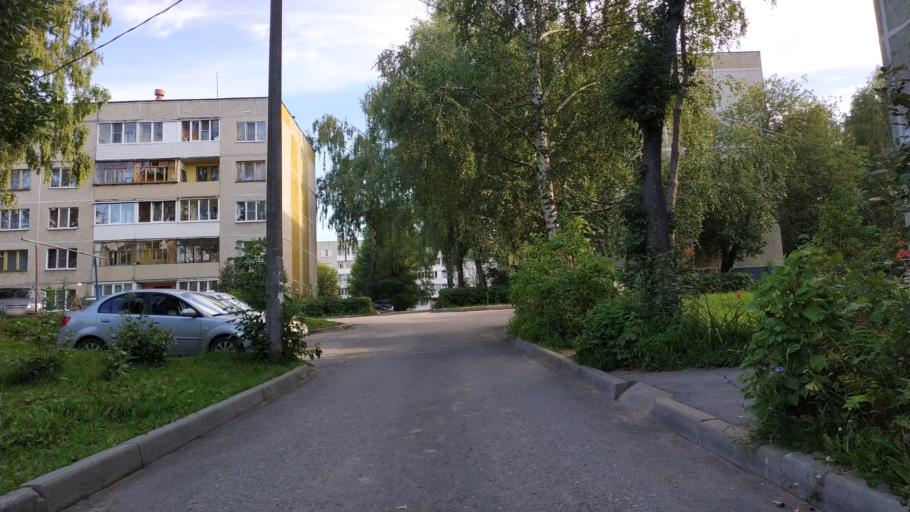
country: RU
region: Chuvashia
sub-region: Cheboksarskiy Rayon
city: Cheboksary
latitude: 56.1444
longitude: 47.1827
